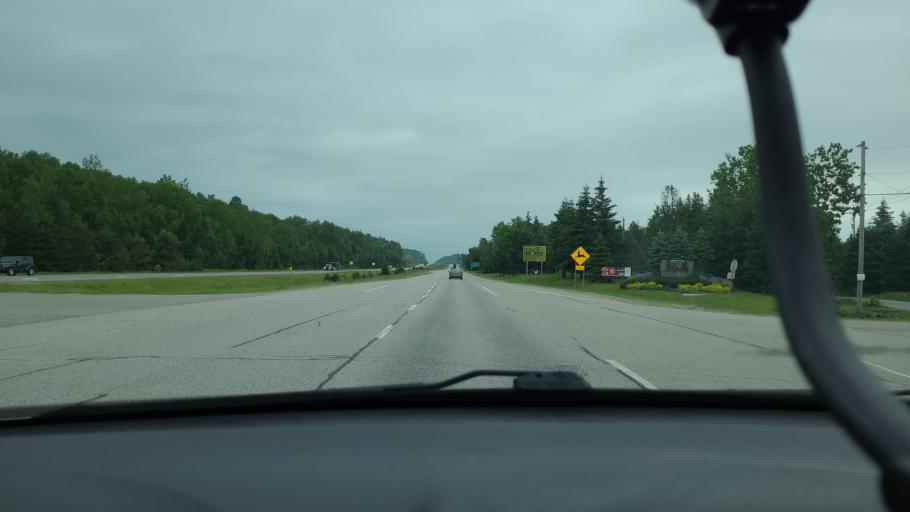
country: CA
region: Quebec
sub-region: Laurentides
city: Labelle
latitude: 46.2452
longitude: -74.7149
